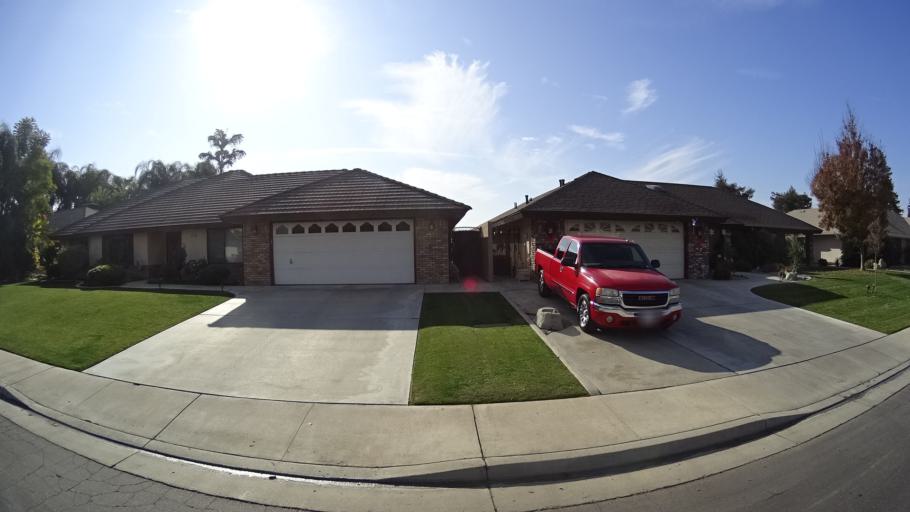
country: US
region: California
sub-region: Kern County
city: Greenacres
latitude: 35.4074
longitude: -119.0724
